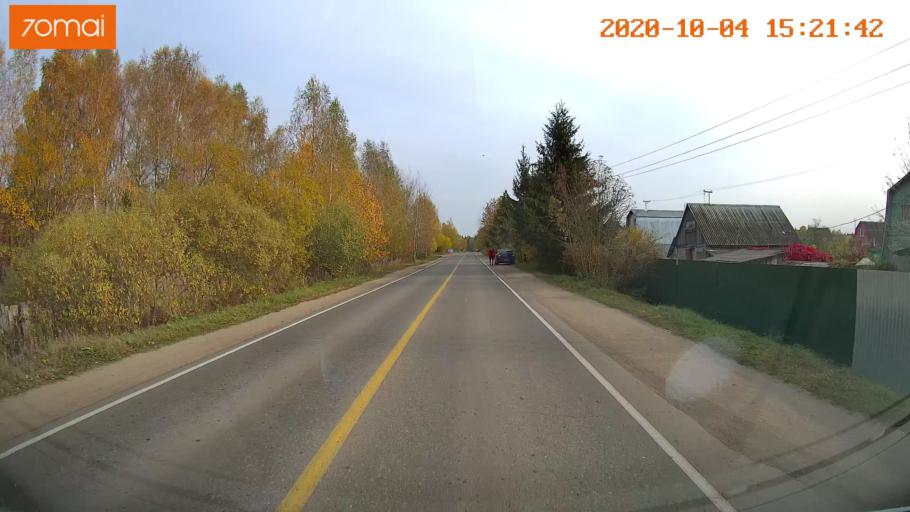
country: RU
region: Ivanovo
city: Bogorodskoye
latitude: 57.0849
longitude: 40.9257
